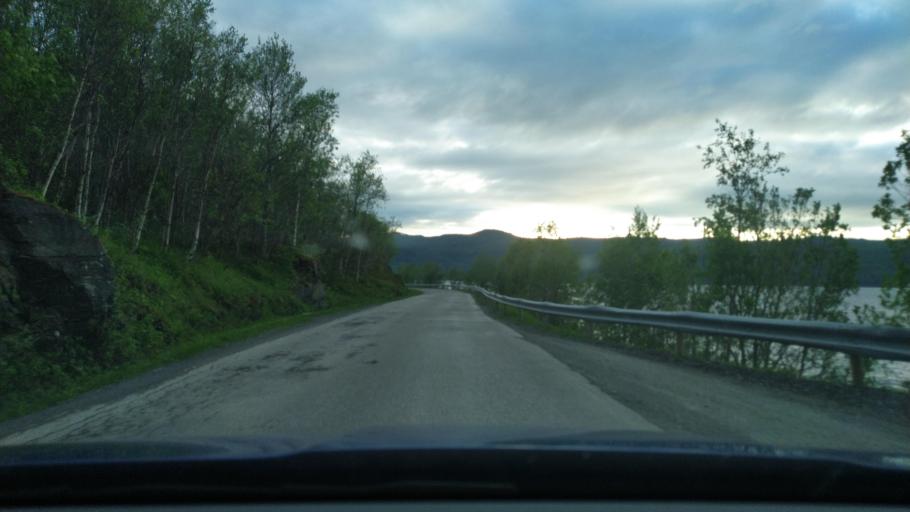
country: NO
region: Troms
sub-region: Lenvik
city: Finnsnes
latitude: 69.1455
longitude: 17.9418
